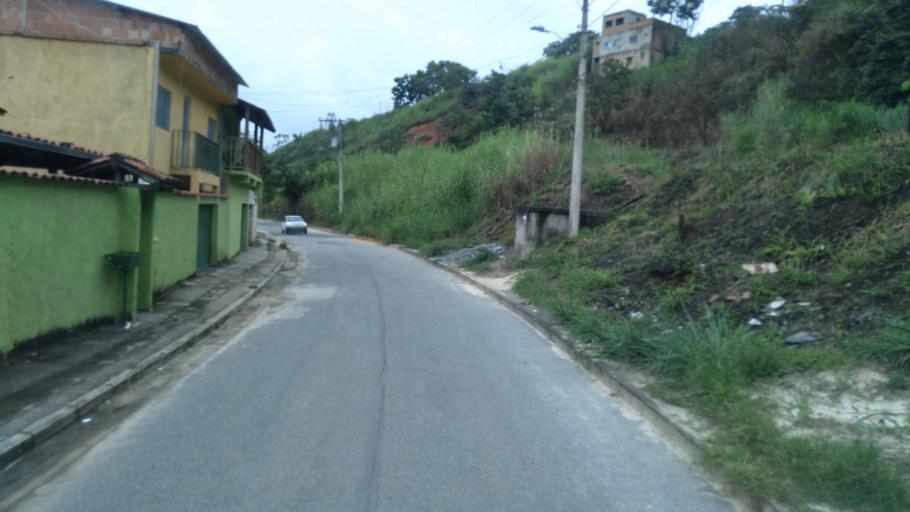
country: BR
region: Minas Gerais
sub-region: Santa Luzia
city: Santa Luzia
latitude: -19.8388
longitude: -43.8705
